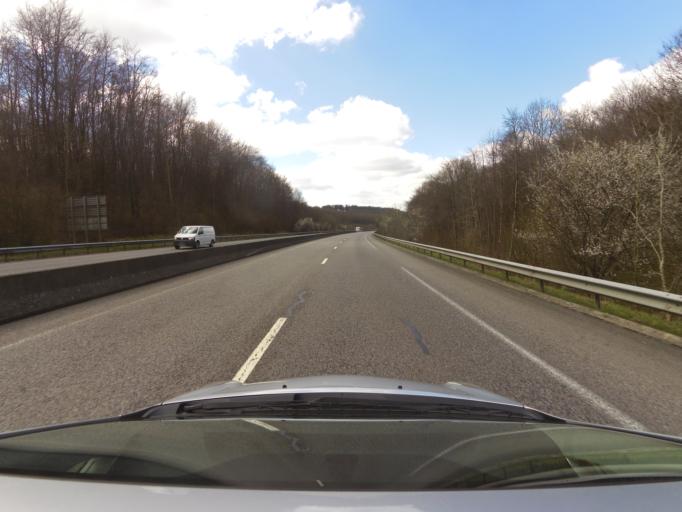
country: FR
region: Haute-Normandie
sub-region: Departement de la Seine-Maritime
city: Foucarmont
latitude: 49.8835
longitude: 1.5962
